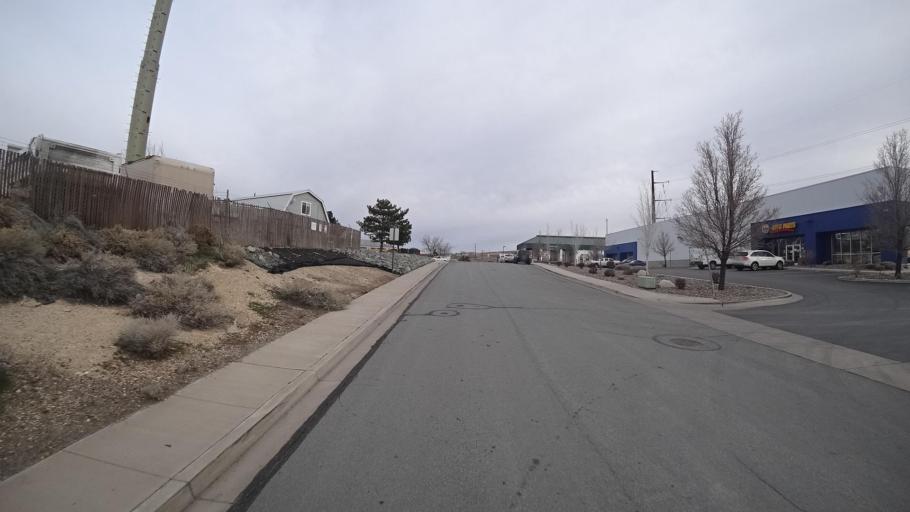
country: US
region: Nevada
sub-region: Washoe County
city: Sun Valley
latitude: 39.5712
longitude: -119.8086
